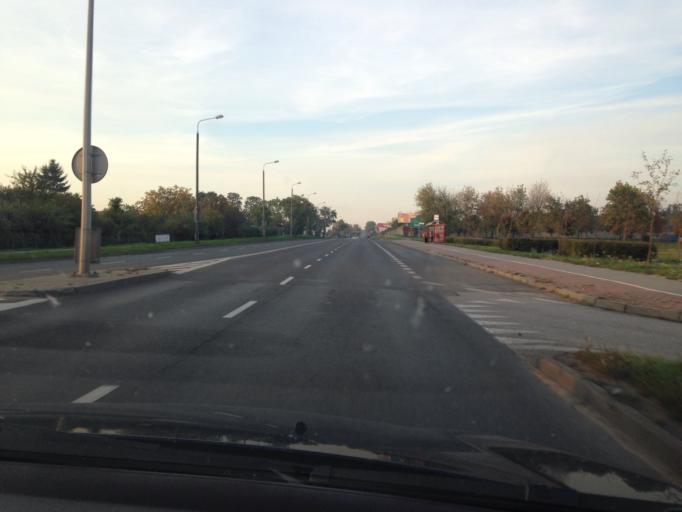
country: PL
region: Kujawsko-Pomorskie
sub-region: Powiat inowroclawski
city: Inowroclaw
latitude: 52.7808
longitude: 18.2601
